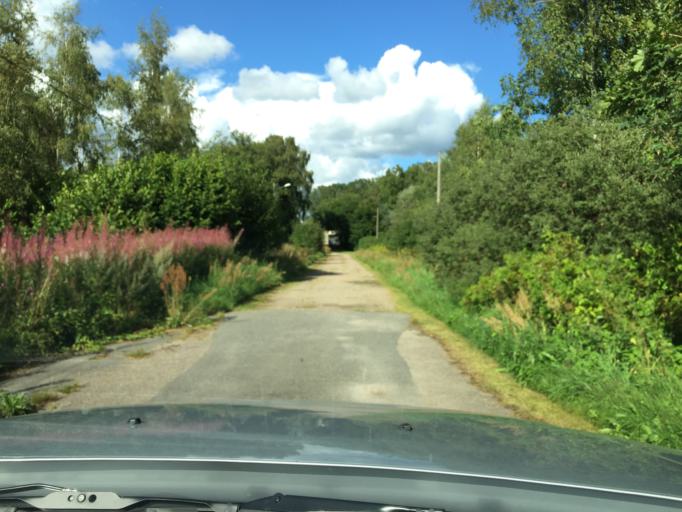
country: SE
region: Skane
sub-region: Hassleholms Kommun
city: Sosdala
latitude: 56.0296
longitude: 13.6863
